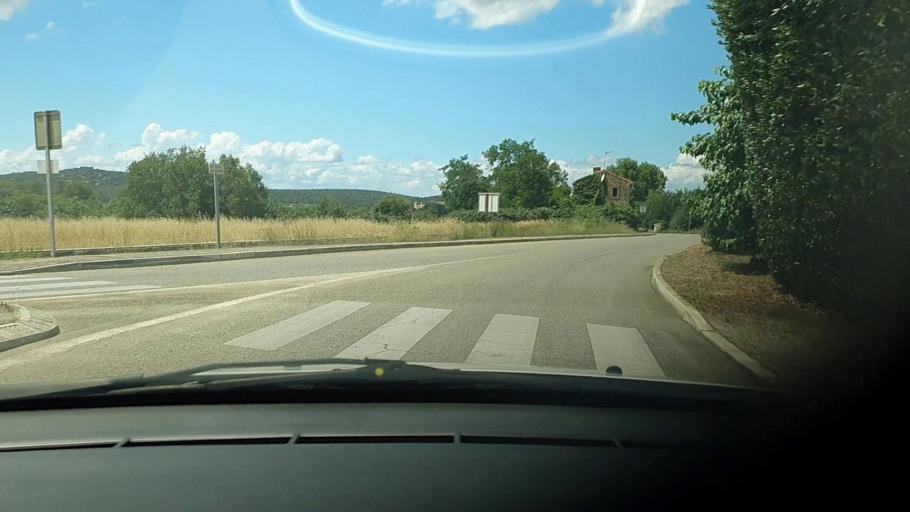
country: FR
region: Languedoc-Roussillon
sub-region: Departement du Gard
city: Saint-Chaptes
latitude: 44.0445
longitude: 4.2992
